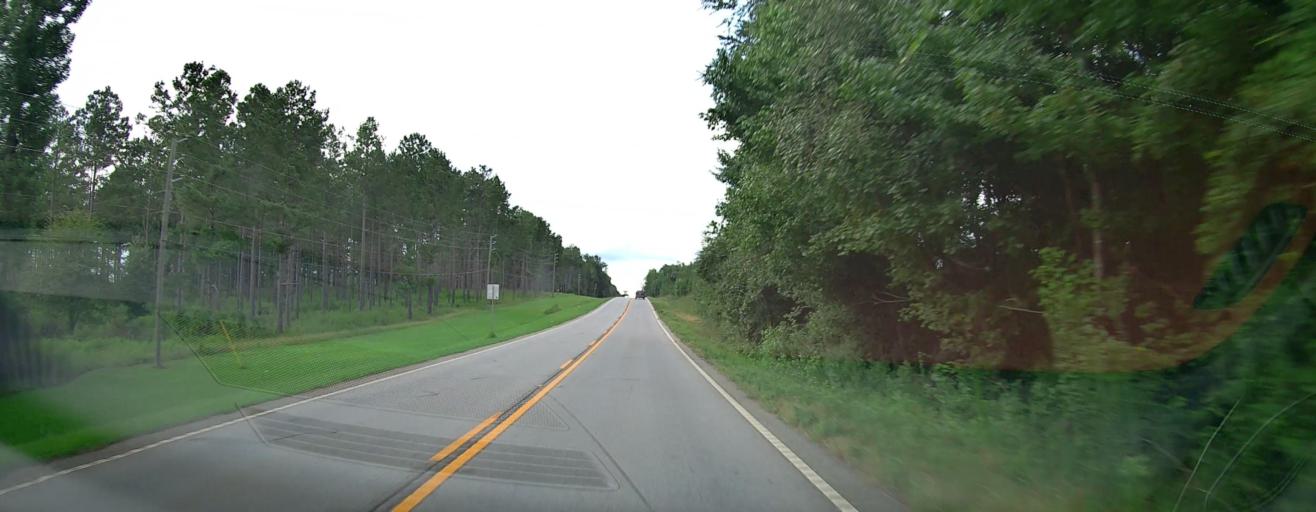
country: US
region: Georgia
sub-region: Meriwether County
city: Greenville
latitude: 33.0533
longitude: -84.5687
